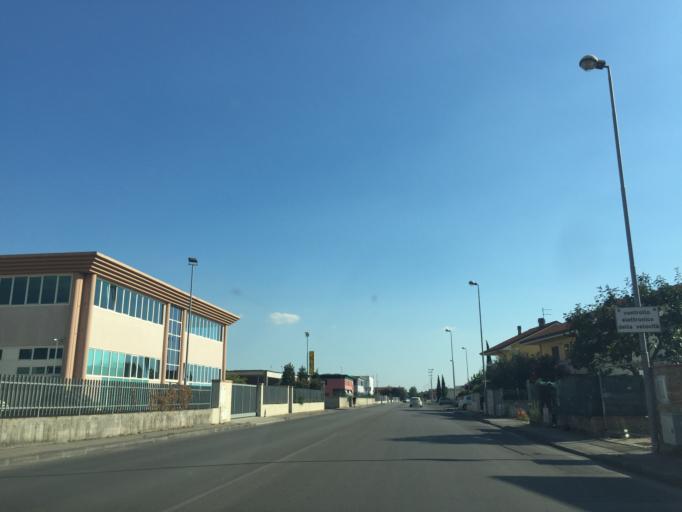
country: IT
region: Tuscany
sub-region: Provincia di Pistoia
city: Monsummano Terme
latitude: 43.8638
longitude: 10.8048
